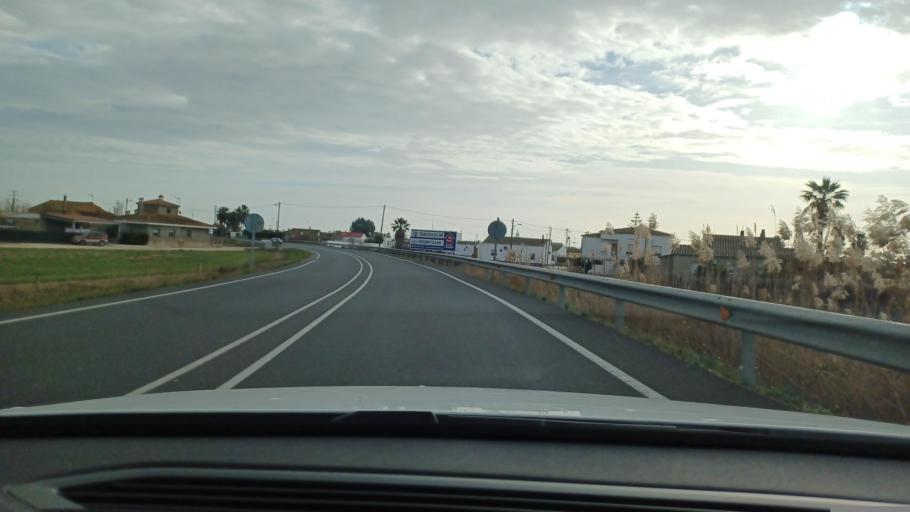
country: ES
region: Catalonia
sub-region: Provincia de Tarragona
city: Deltebre
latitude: 40.7290
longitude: 0.6859
